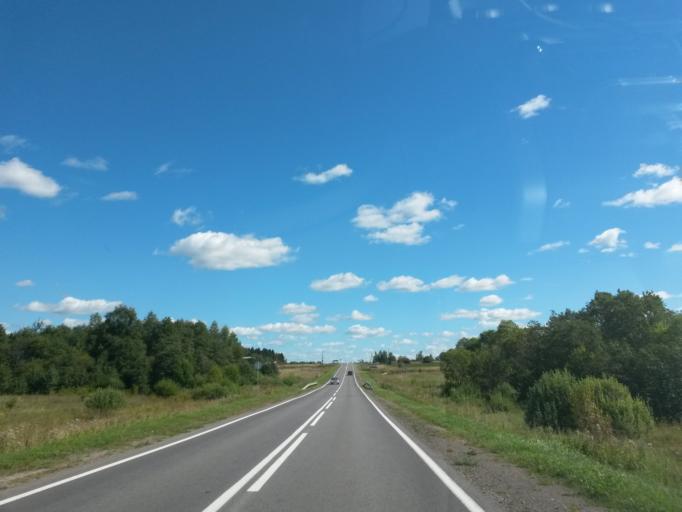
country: RU
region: Jaroslavl
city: Konstantinovskiy
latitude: 57.8214
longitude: 39.6900
